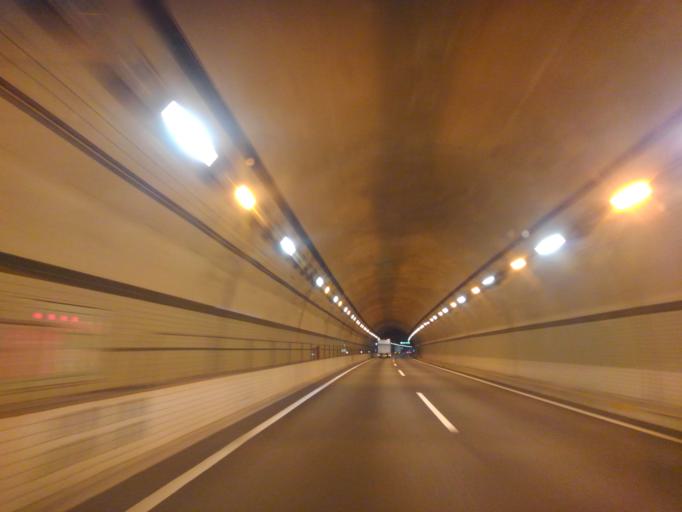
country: JP
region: Tokyo
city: Itsukaichi
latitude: 35.6941
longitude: 139.2663
